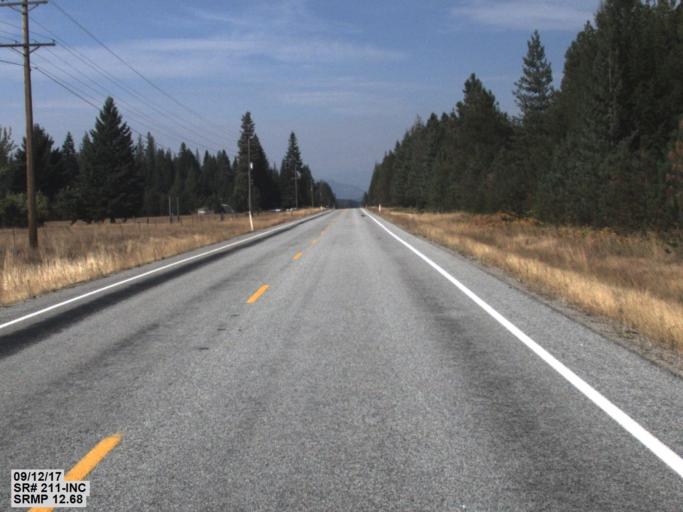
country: US
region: Washington
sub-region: Pend Oreille County
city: Newport
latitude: 48.2689
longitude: -117.2845
